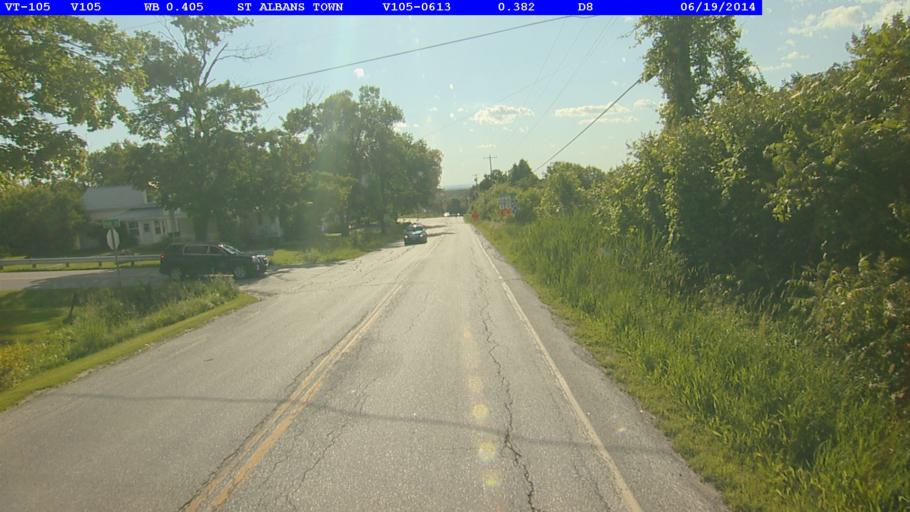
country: US
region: Vermont
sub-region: Franklin County
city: Saint Albans
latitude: 44.8273
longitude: -73.0752
